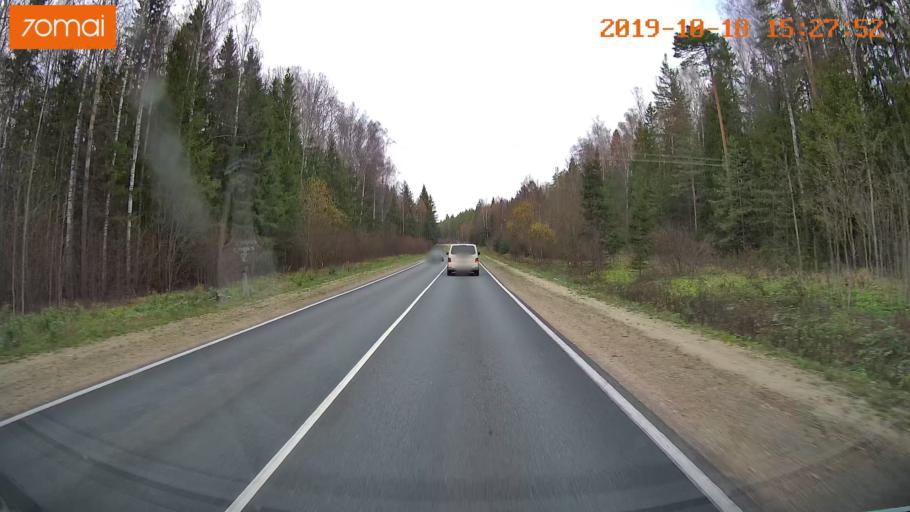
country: RU
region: Vladimir
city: Anopino
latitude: 55.7591
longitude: 40.6726
